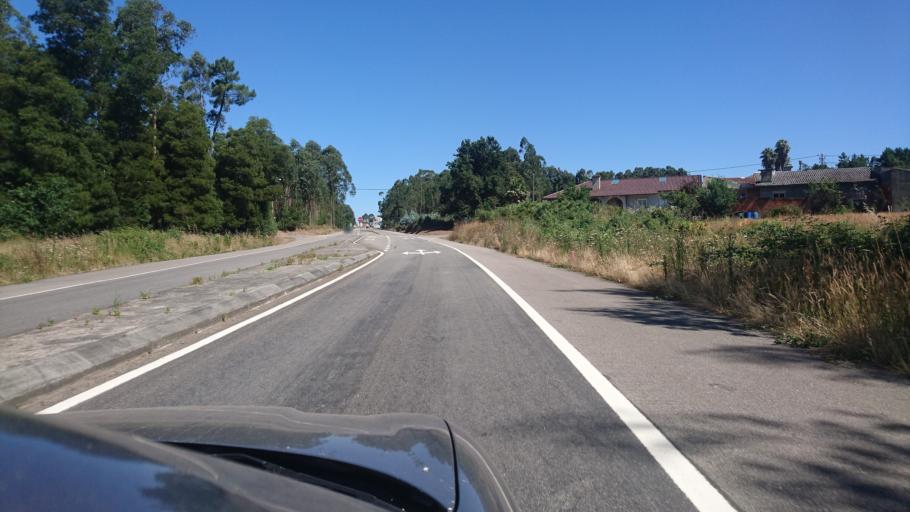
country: PT
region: Aveiro
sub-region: Santa Maria da Feira
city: Rio Meao
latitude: 40.9522
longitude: -8.5863
